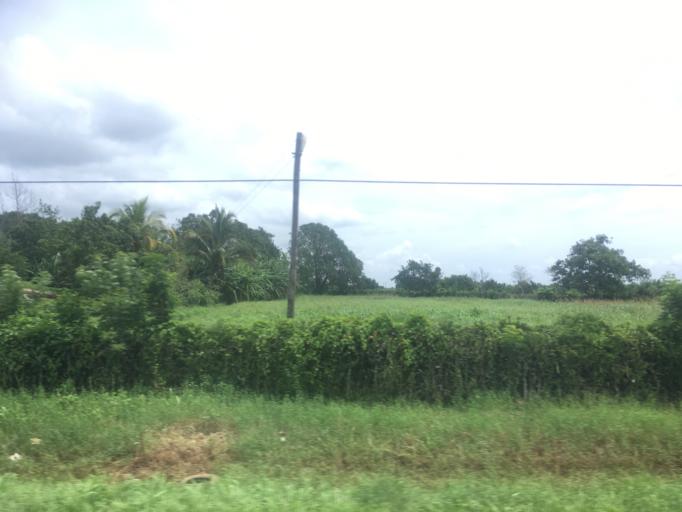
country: CU
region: Matanzas
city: Jovellanos
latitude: 22.7980
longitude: -81.1585
